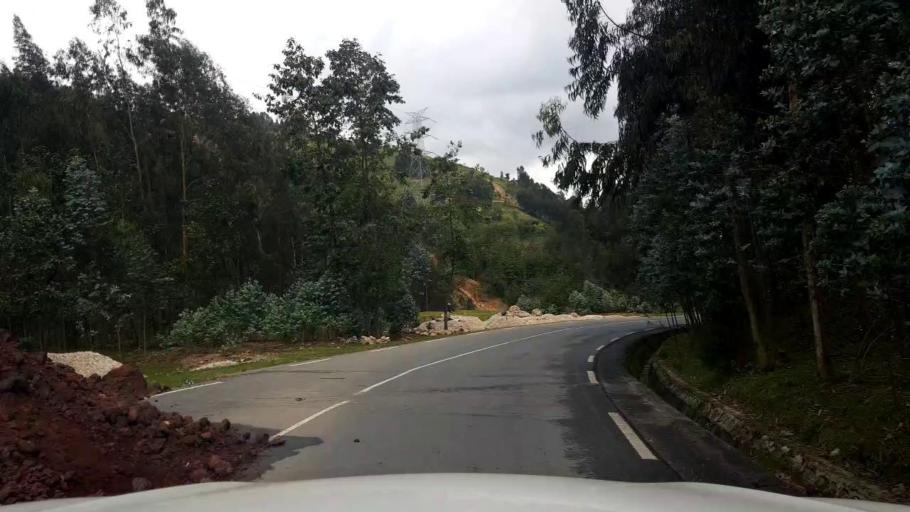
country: RW
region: Northern Province
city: Musanze
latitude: -1.6840
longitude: 29.5317
